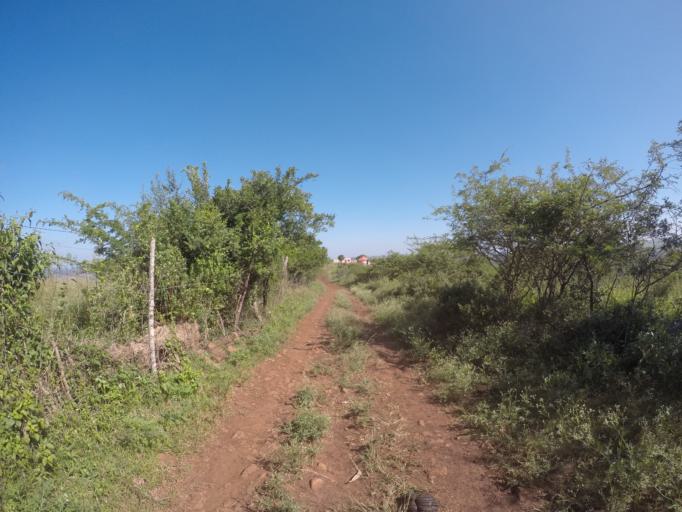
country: ZA
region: KwaZulu-Natal
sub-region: uThungulu District Municipality
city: Empangeni
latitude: -28.5714
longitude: 31.7102
